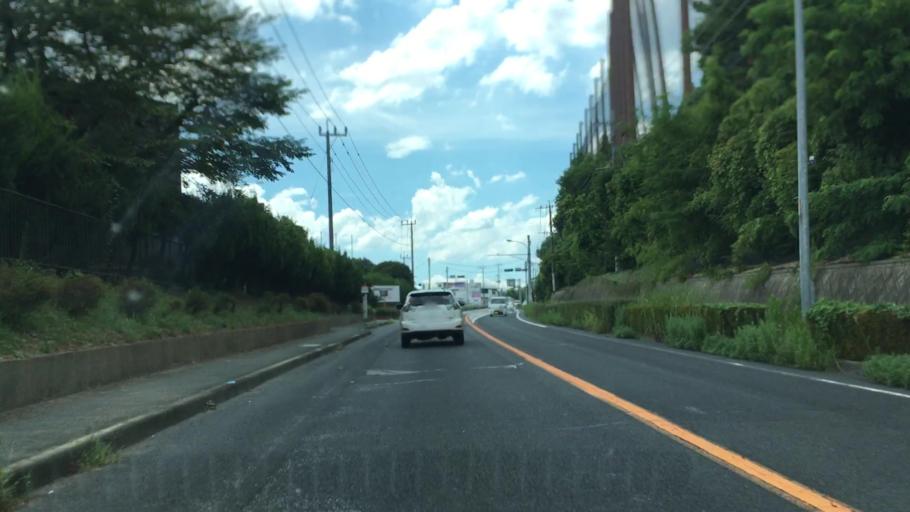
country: JP
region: Saga Prefecture
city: Tosu
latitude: 33.3601
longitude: 130.4947
